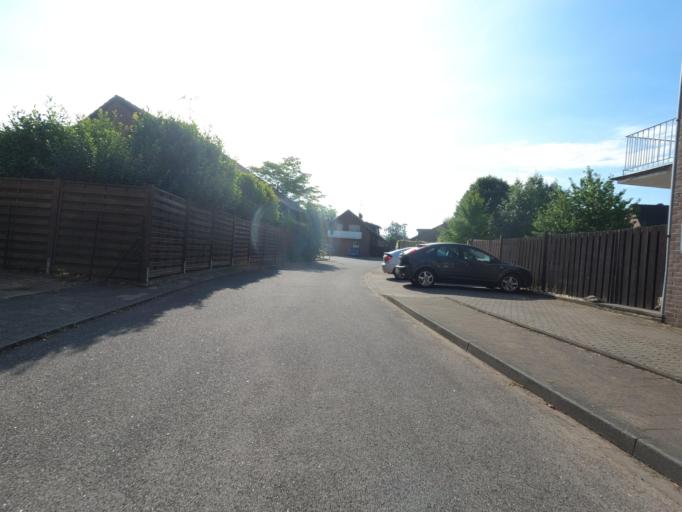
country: DE
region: North Rhine-Westphalia
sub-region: Regierungsbezirk Koln
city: Wassenberg
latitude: 51.0602
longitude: 6.1451
